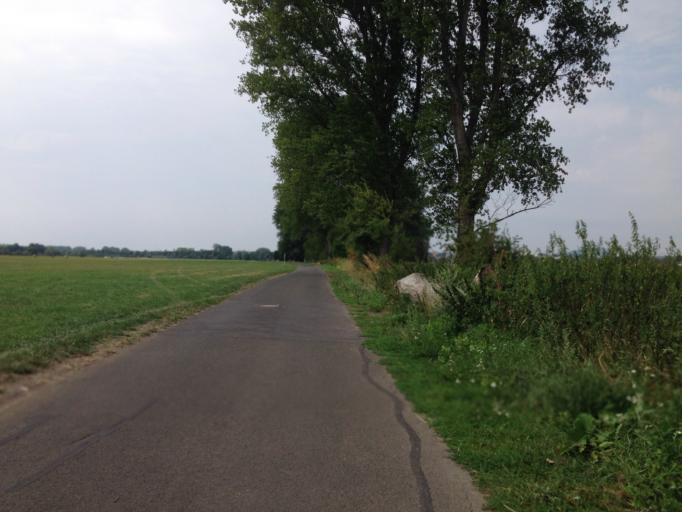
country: DE
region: Hesse
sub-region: Regierungsbezirk Giessen
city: Alten Buseck
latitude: 50.6055
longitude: 8.7359
